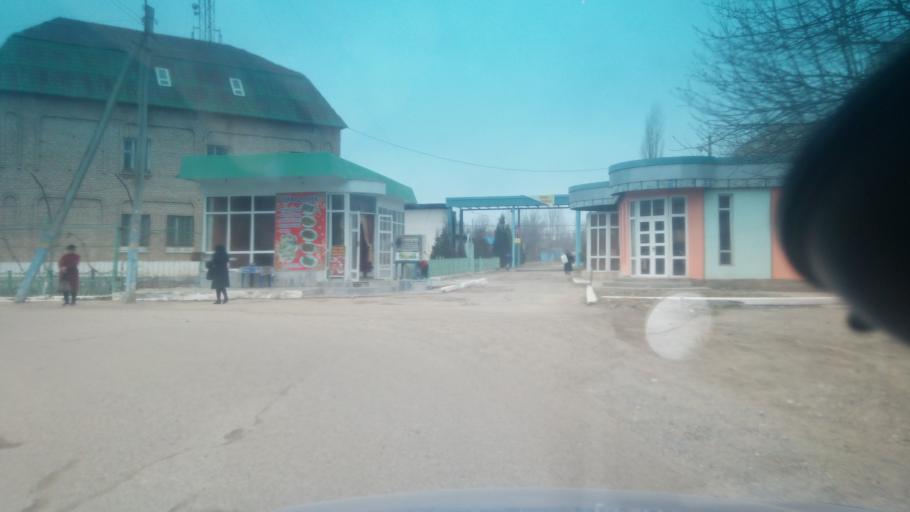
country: UZ
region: Sirdaryo
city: Guliston
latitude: 40.5179
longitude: 68.7783
